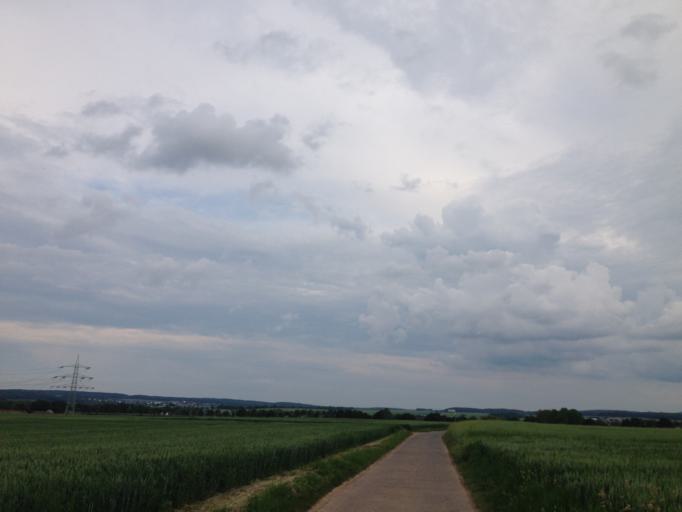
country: DE
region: Hesse
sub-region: Regierungsbezirk Giessen
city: Hoernsheim
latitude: 50.5313
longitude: 8.6260
